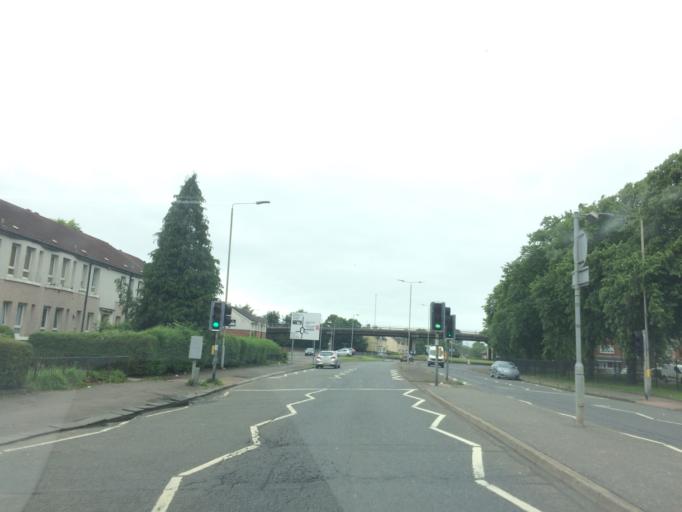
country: GB
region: Scotland
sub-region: Renfrewshire
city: Renfrew
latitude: 55.8562
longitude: -4.3377
